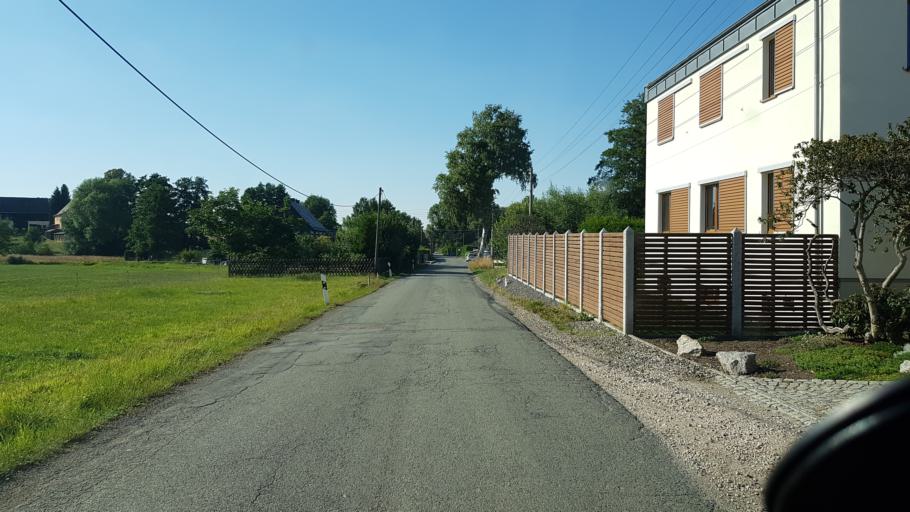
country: DE
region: Saxony
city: Hirschfeld
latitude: 50.6576
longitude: 12.4394
